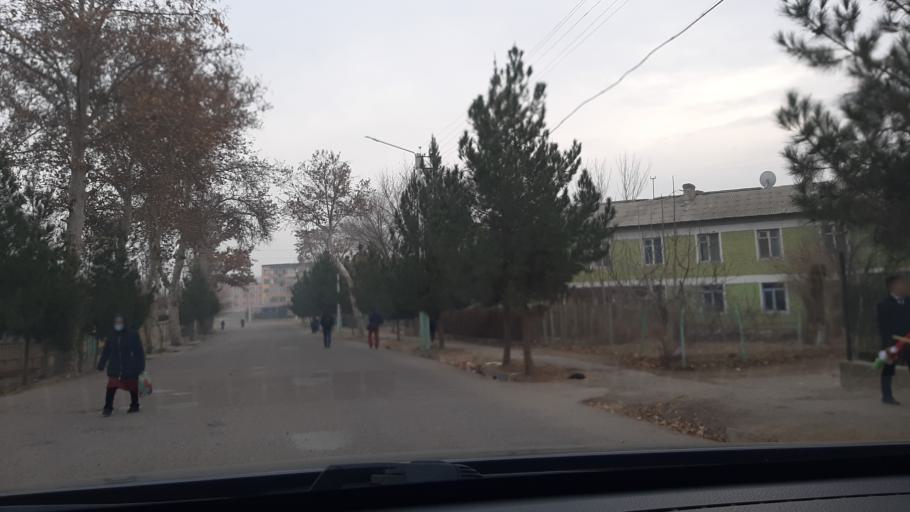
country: TJ
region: Viloyati Sughd
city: Palos
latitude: 40.2627
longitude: 69.7905
